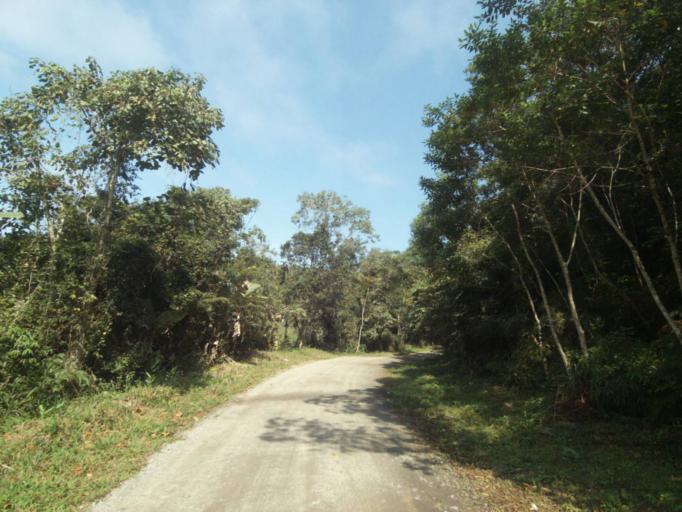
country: BR
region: Parana
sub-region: Paranagua
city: Paranagua
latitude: -25.5574
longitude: -48.6477
